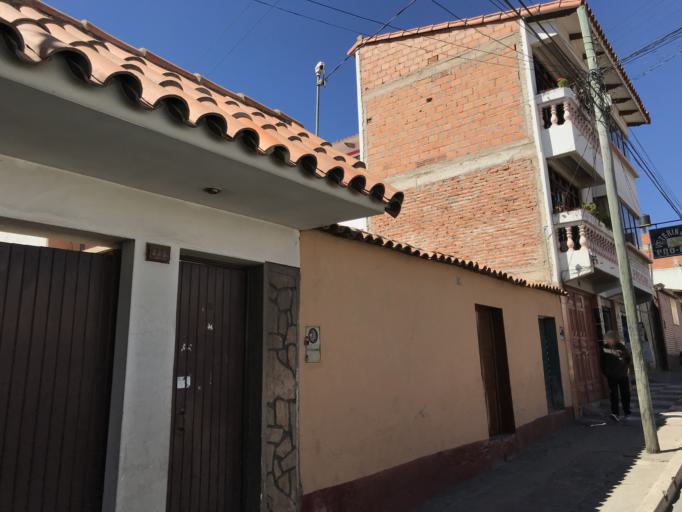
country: BO
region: Chuquisaca
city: Sucre
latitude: -19.0391
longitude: -65.2495
